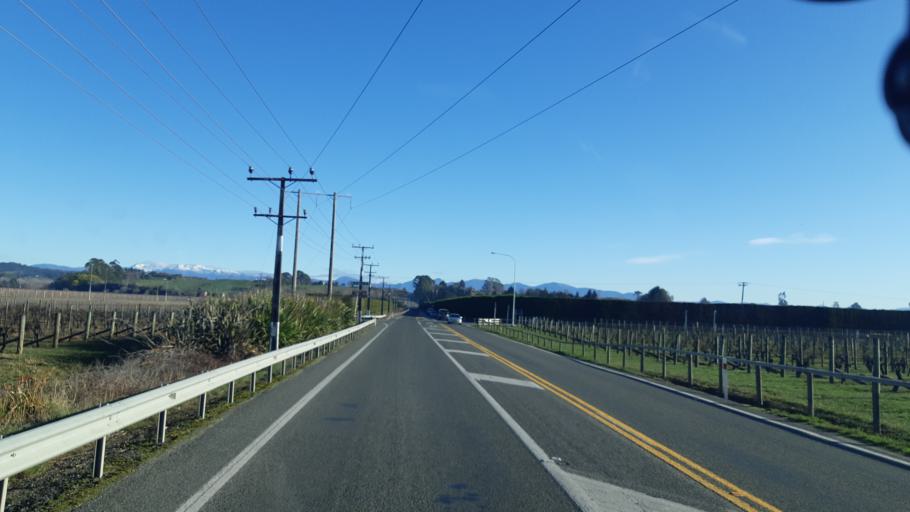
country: NZ
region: Tasman
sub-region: Tasman District
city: Mapua
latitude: -41.3031
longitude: 173.1152
